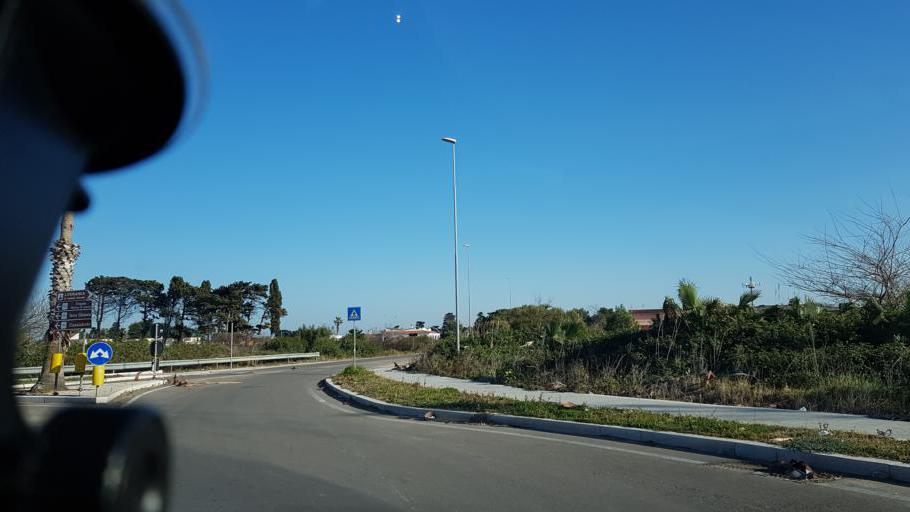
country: IT
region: Apulia
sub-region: Provincia di Lecce
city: Merine
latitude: 40.4271
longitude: 18.2434
